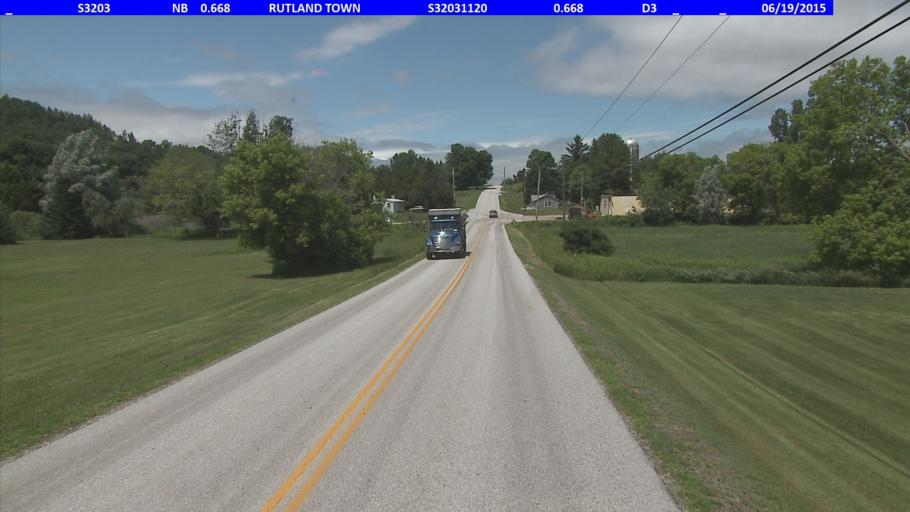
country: US
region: Vermont
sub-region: Rutland County
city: Rutland
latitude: 43.6627
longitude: -72.9998
